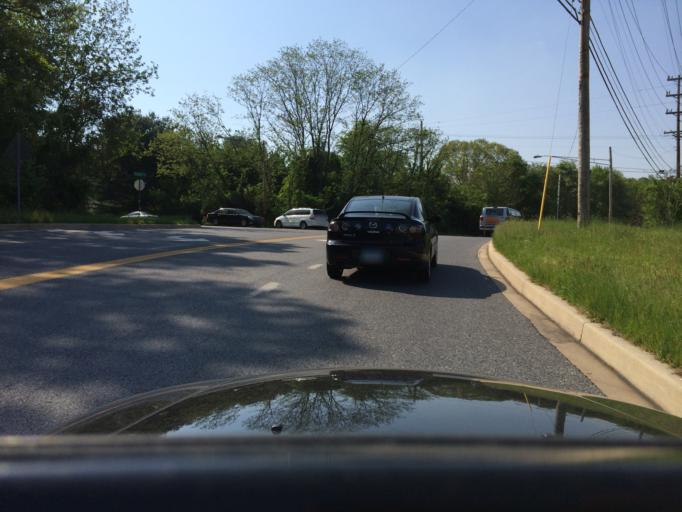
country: US
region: Maryland
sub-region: Howard County
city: Riverside
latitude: 39.1813
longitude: -76.8999
